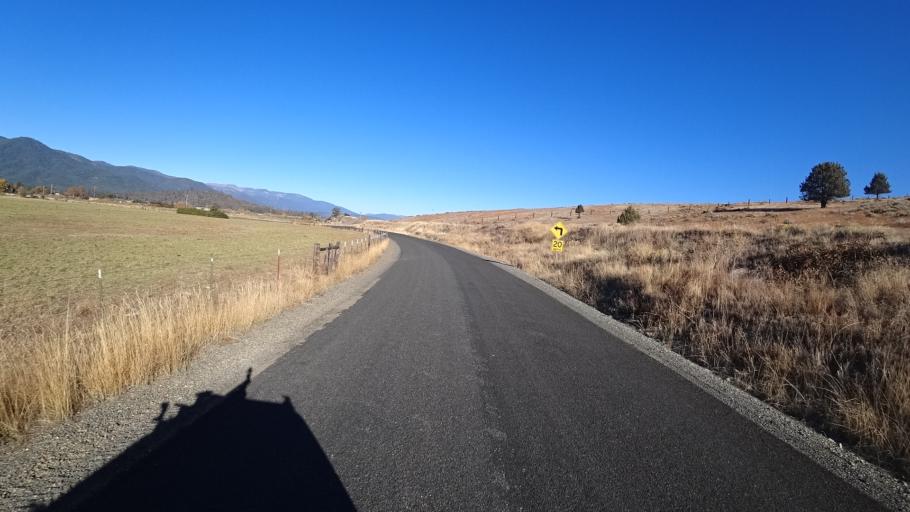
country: US
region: California
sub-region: Siskiyou County
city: Yreka
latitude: 41.4567
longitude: -122.8461
